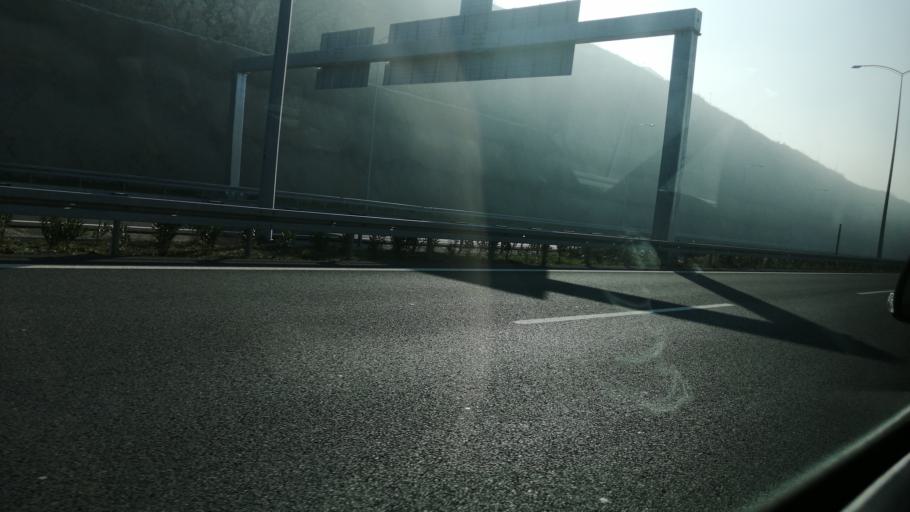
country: TR
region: Kocaeli
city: Tavsanli
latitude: 40.7796
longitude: 29.5176
